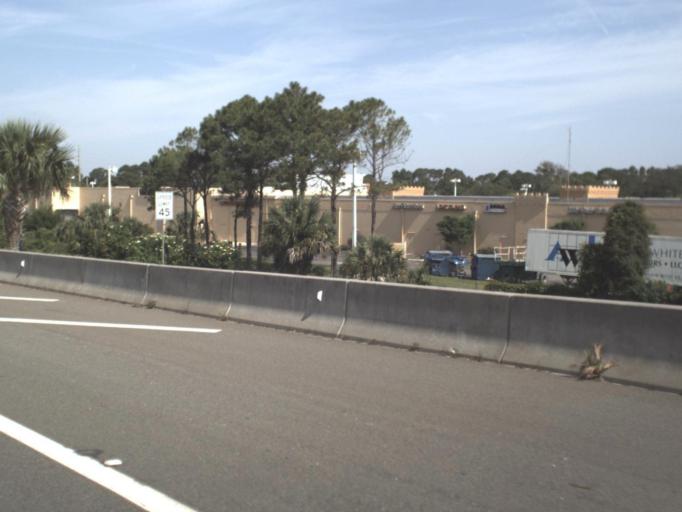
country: US
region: Florida
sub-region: Saint Johns County
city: Ponte Vedra Beach
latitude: 30.2561
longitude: -81.3901
